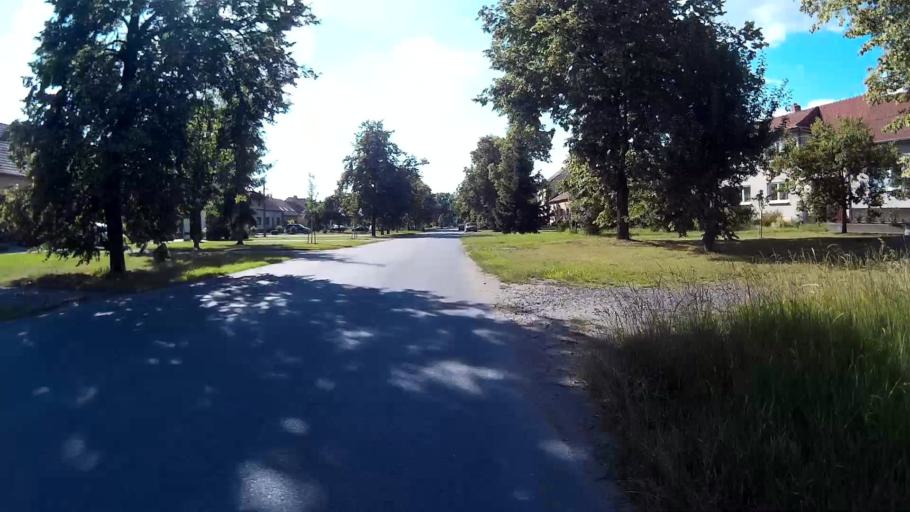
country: CZ
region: South Moravian
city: Tesany
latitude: 49.0425
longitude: 16.7678
